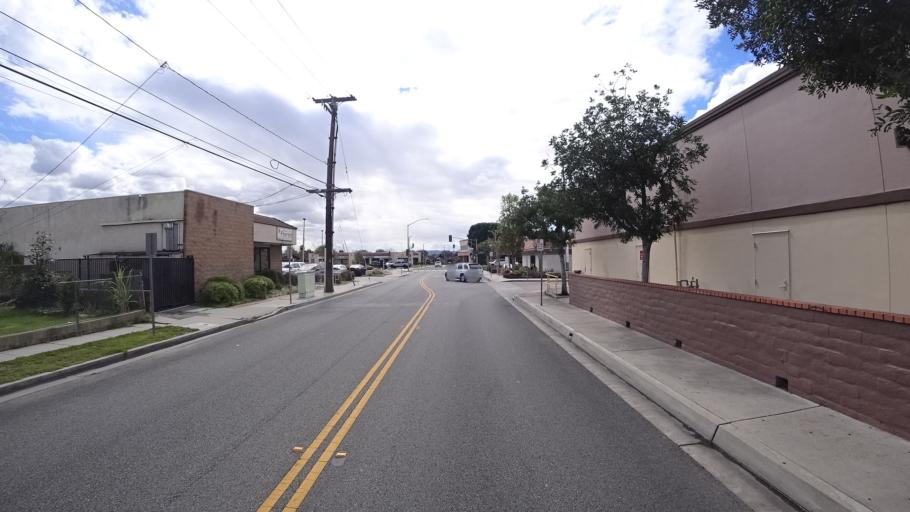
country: US
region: California
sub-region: Los Angeles County
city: Baldwin Park
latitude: 34.0880
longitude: -117.9578
